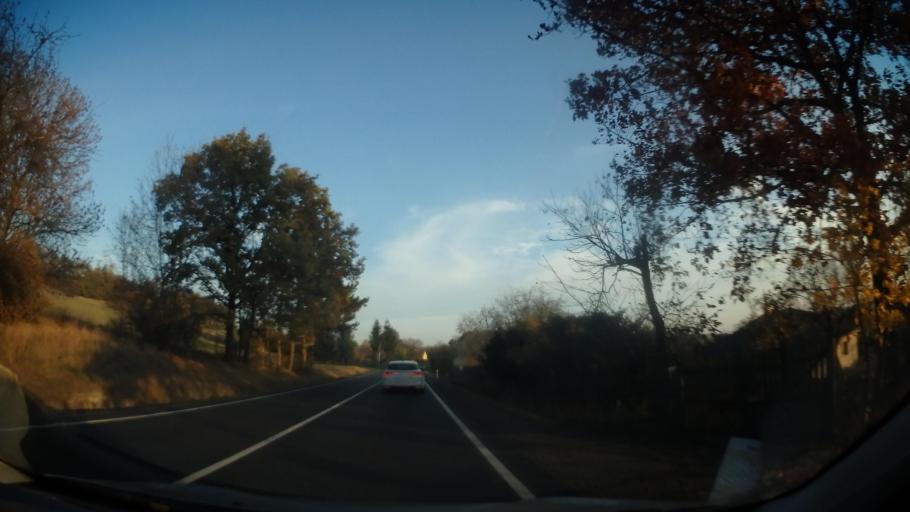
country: CZ
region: Central Bohemia
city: Postupice
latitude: 49.7471
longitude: 14.7917
